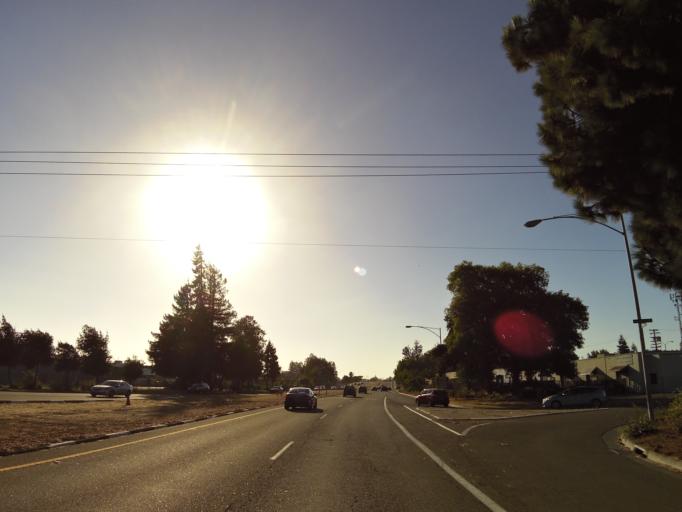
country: US
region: California
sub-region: Santa Clara County
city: Sunnyvale
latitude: 37.3768
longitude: -122.0079
